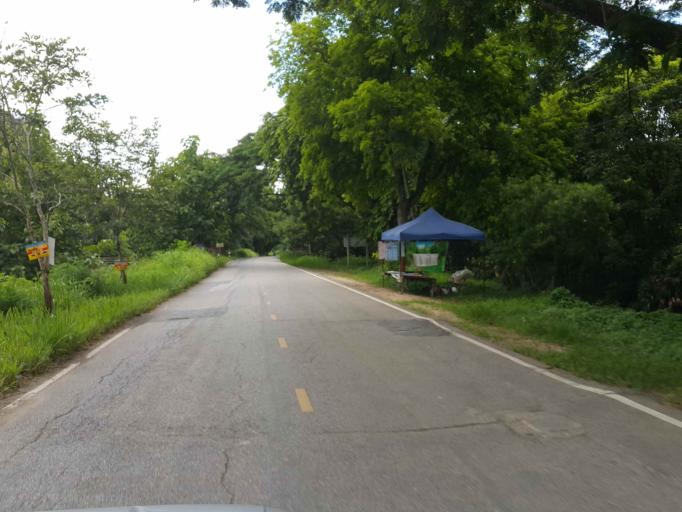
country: TH
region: Chiang Mai
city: San Sai
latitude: 18.9092
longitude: 98.9421
